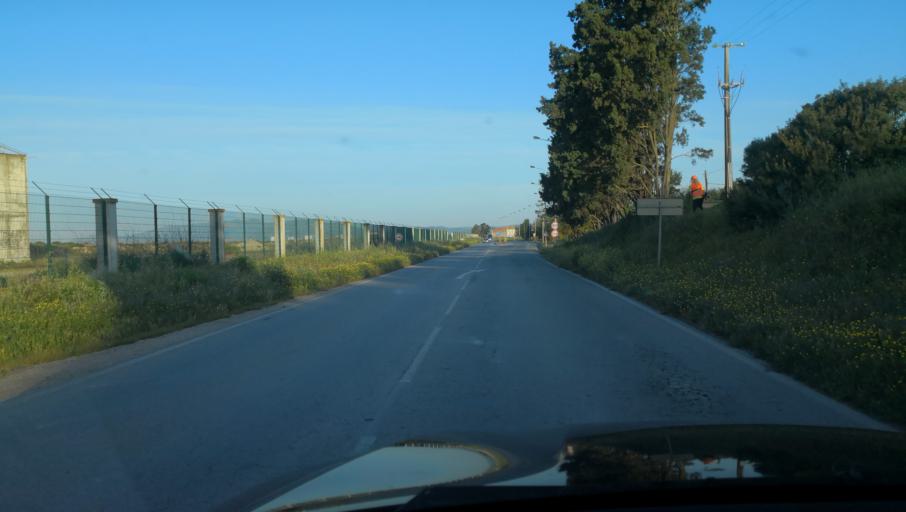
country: PT
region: Setubal
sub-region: Setubal
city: Setubal
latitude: 38.4927
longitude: -8.8254
